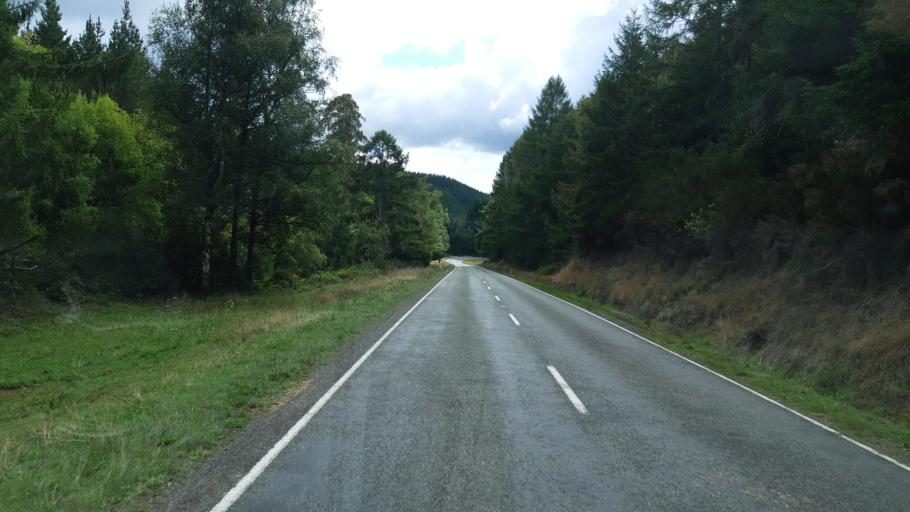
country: NZ
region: Tasman
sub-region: Tasman District
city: Wakefield
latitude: -41.6065
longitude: 172.7593
